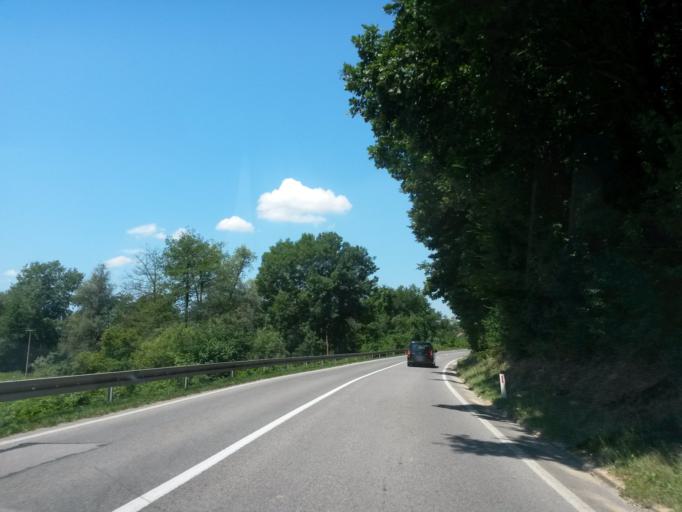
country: BA
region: Federation of Bosnia and Herzegovina
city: Lukavica
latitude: 44.9302
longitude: 18.1568
